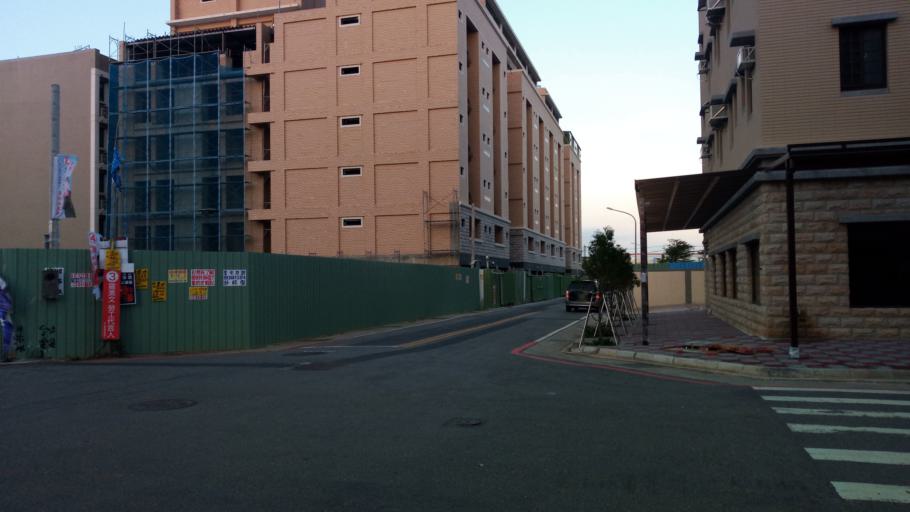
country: TW
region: Taiwan
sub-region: Hsinchu
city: Zhubei
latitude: 24.8643
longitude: 120.9967
